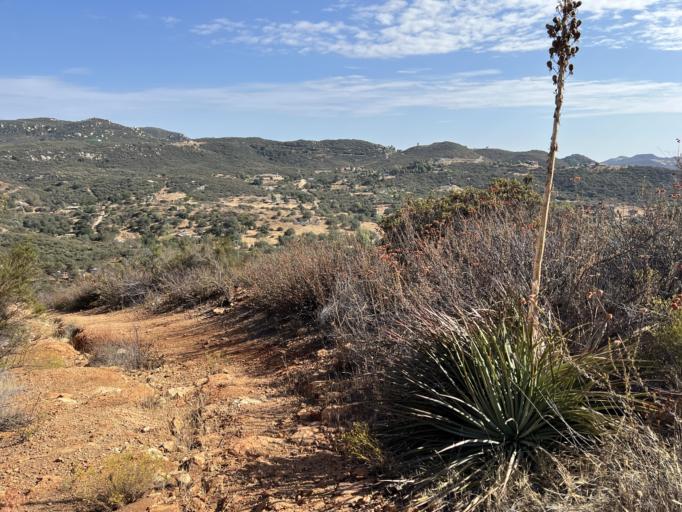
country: US
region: California
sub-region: San Diego County
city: Harbison Canyon
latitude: 32.7482
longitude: -116.8000
